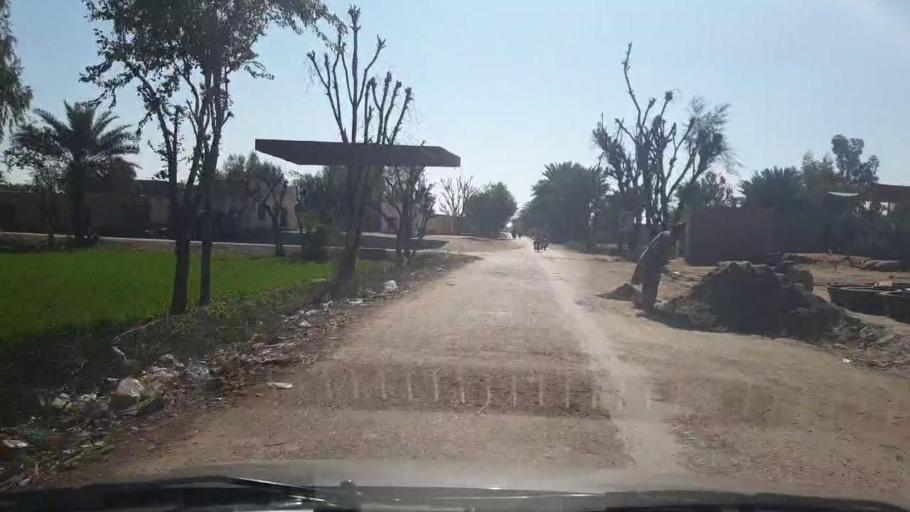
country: PK
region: Sindh
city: Bozdar
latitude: 27.1764
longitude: 68.6401
